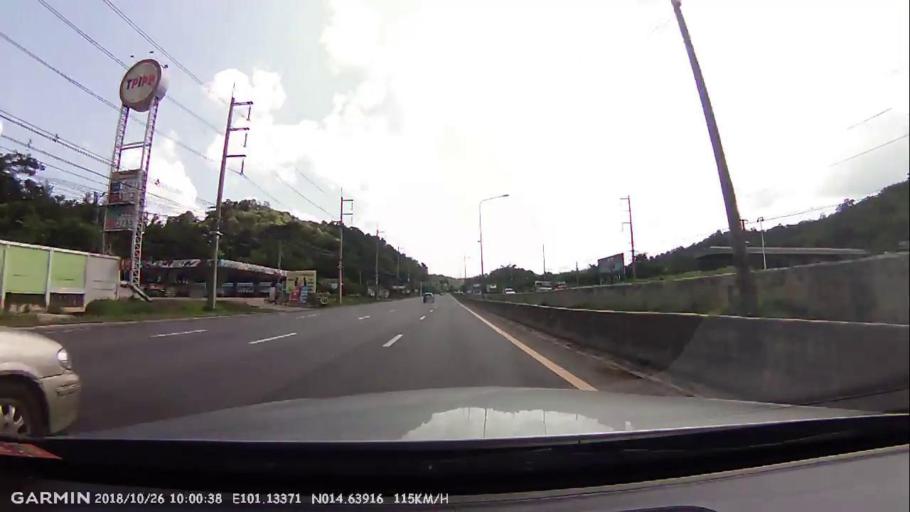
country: TH
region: Sara Buri
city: Muak Lek
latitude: 14.6394
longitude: 101.1338
